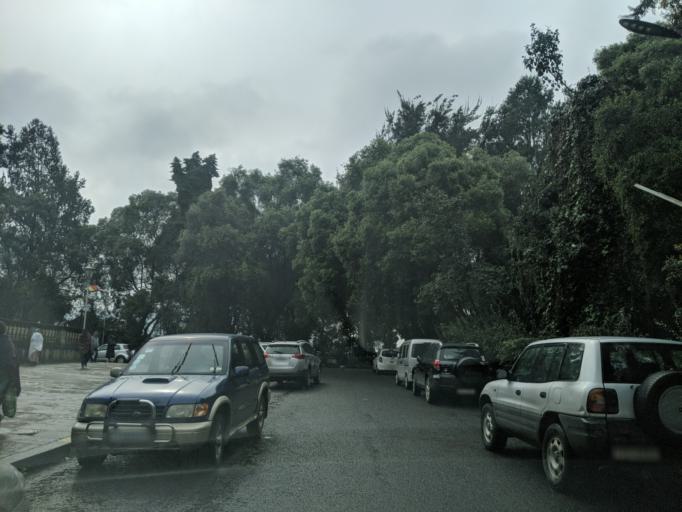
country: ET
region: Adis Abeba
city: Addis Ababa
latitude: 9.0306
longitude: 38.7666
